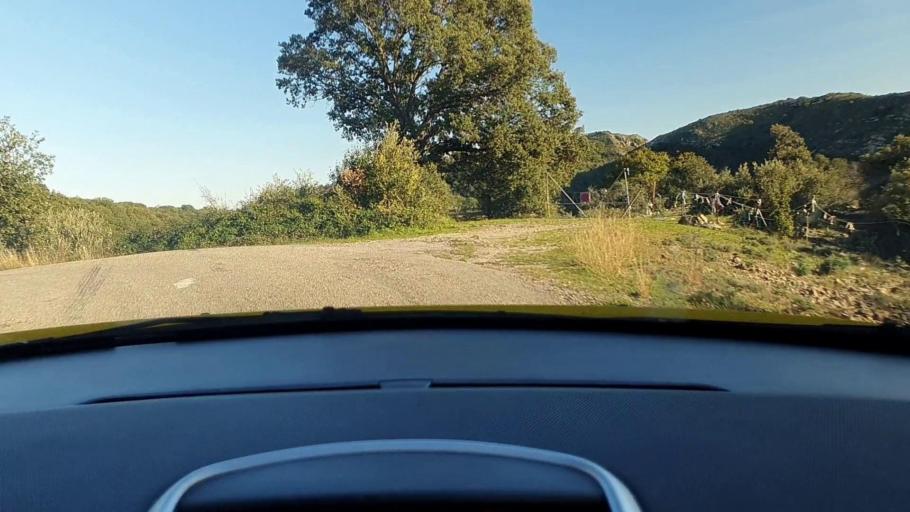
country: FR
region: Languedoc-Roussillon
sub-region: Departement du Gard
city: Sumene
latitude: 43.9767
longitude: 3.7626
